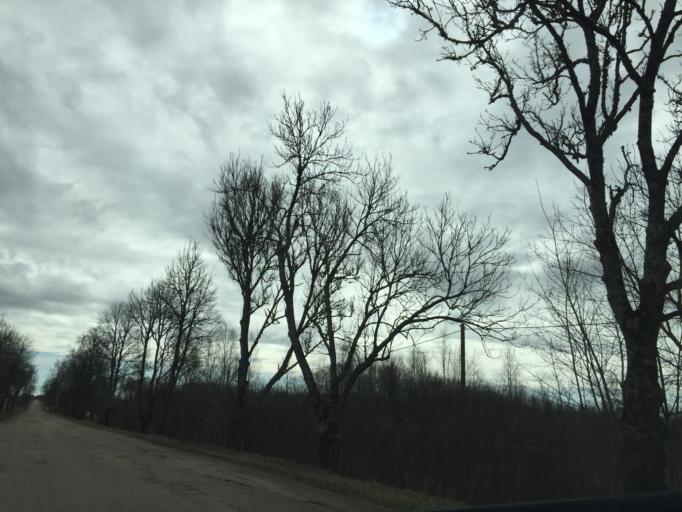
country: LV
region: Daugavpils
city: Daugavpils
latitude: 55.9303
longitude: 26.7183
